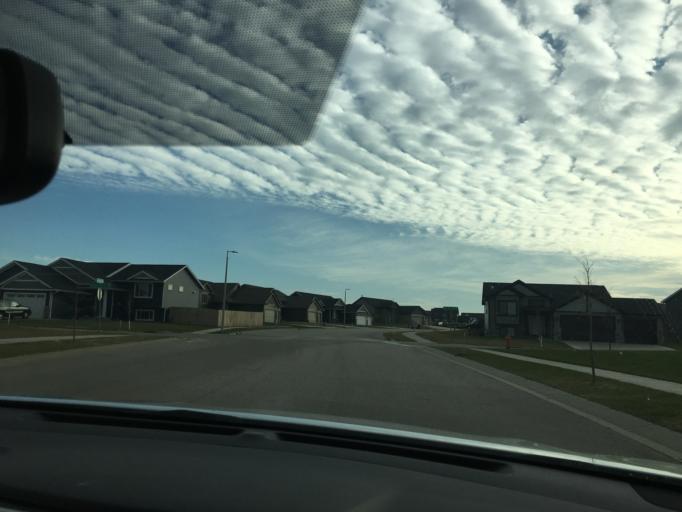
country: US
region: Minnesota
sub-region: Olmsted County
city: Oronoco
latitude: 44.0936
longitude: -92.5258
